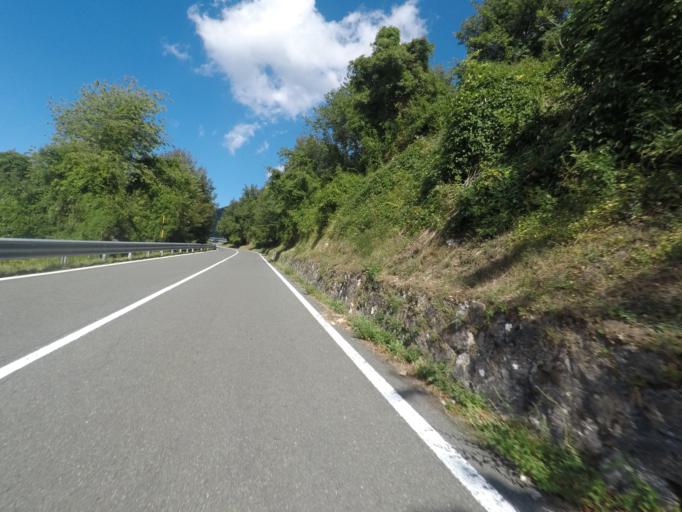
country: IT
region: Tuscany
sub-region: Provincia di Massa-Carrara
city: Comano
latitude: 44.2645
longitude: 10.1716
